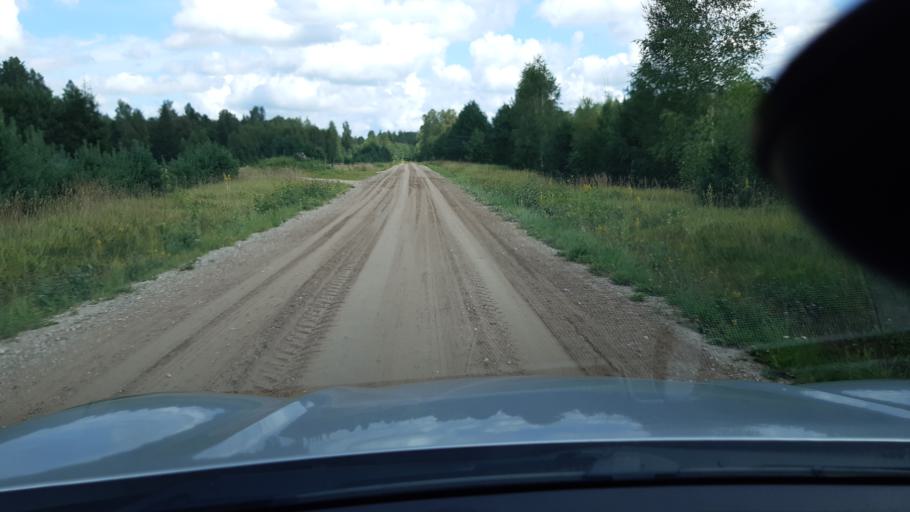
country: EE
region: Jaervamaa
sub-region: Tueri vald
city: Tueri
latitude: 58.9311
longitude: 25.2254
